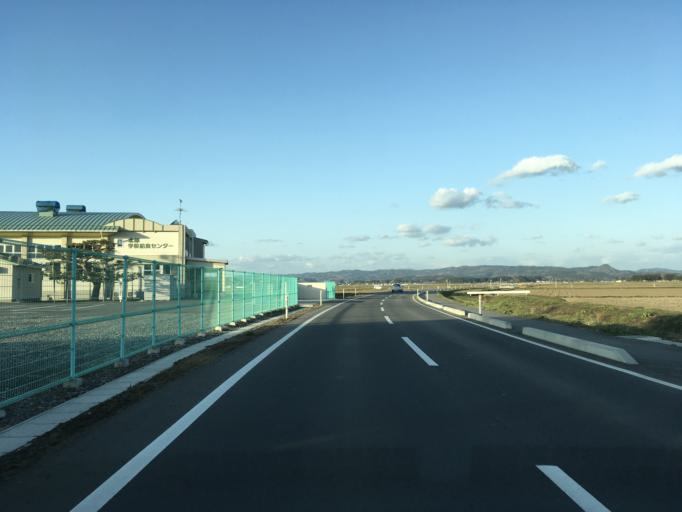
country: JP
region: Miyagi
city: Wakuya
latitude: 38.7145
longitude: 141.2215
